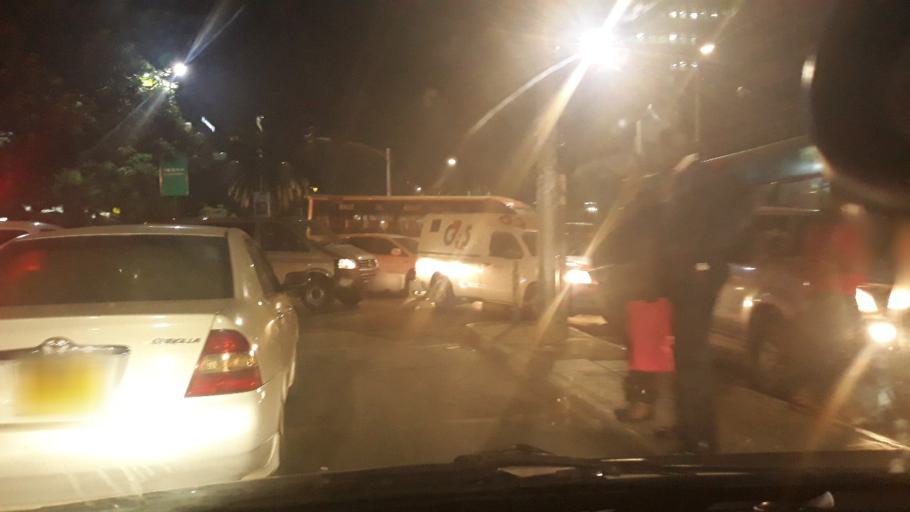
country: KE
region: Nairobi Area
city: Nairobi
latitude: -1.2879
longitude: 36.8268
